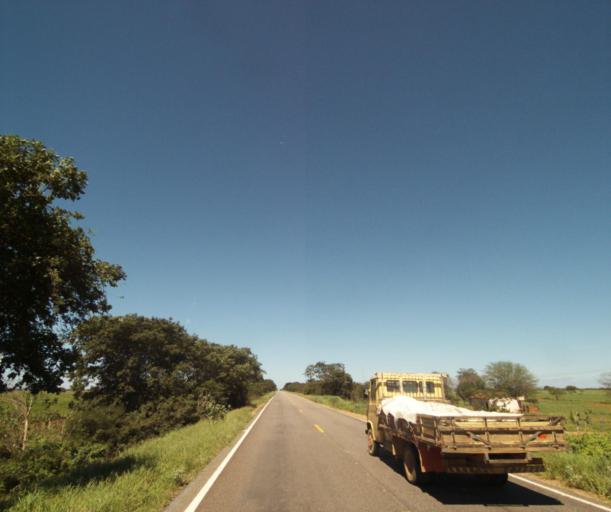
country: BR
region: Bahia
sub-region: Palmas De Monte Alto
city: Palmas de Monte Alto
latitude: -14.2646
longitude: -43.3468
